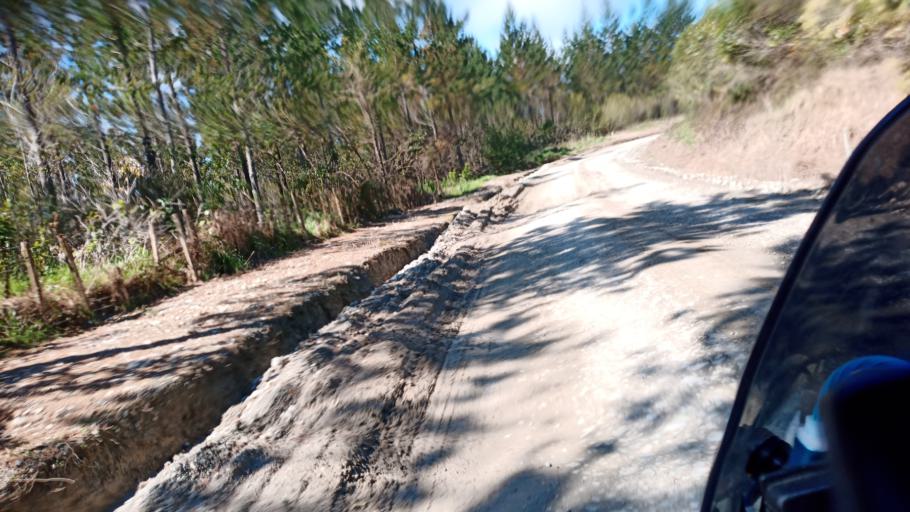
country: NZ
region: Gisborne
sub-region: Gisborne District
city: Gisborne
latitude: -38.9076
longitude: 177.8126
